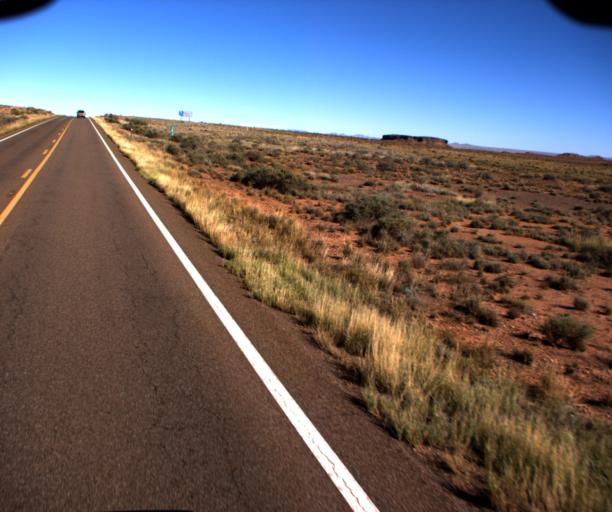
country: US
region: Arizona
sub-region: Navajo County
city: Holbrook
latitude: 34.8244
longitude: -110.1417
